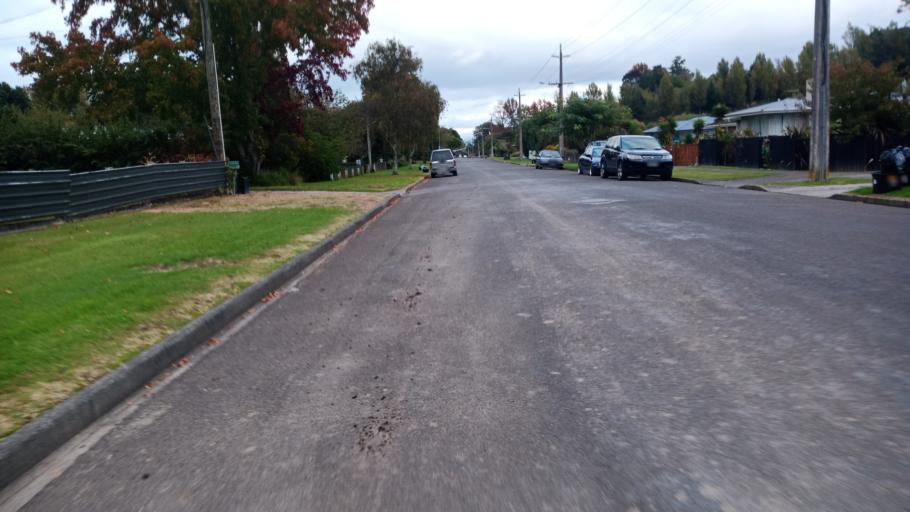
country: NZ
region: Gisborne
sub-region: Gisborne District
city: Gisborne
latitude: -38.6448
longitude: 178.0263
